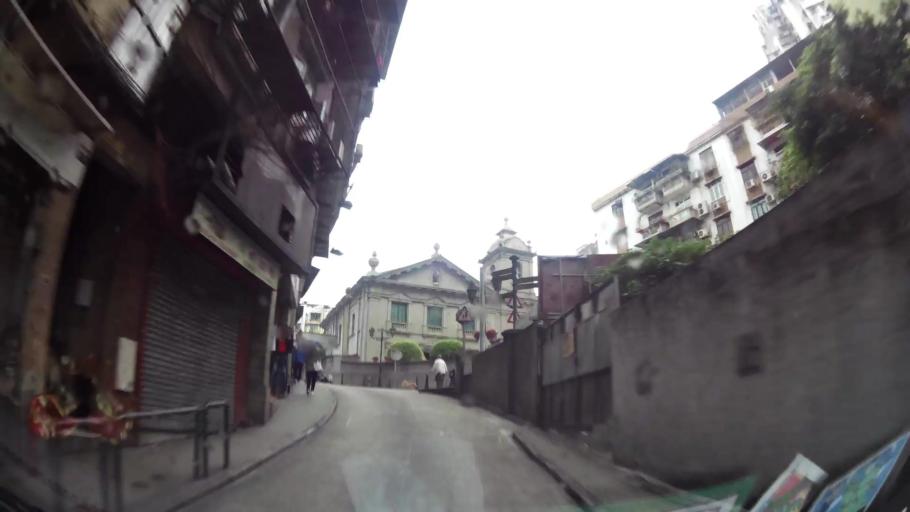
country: MO
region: Macau
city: Macau
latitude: 22.1989
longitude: 113.5389
